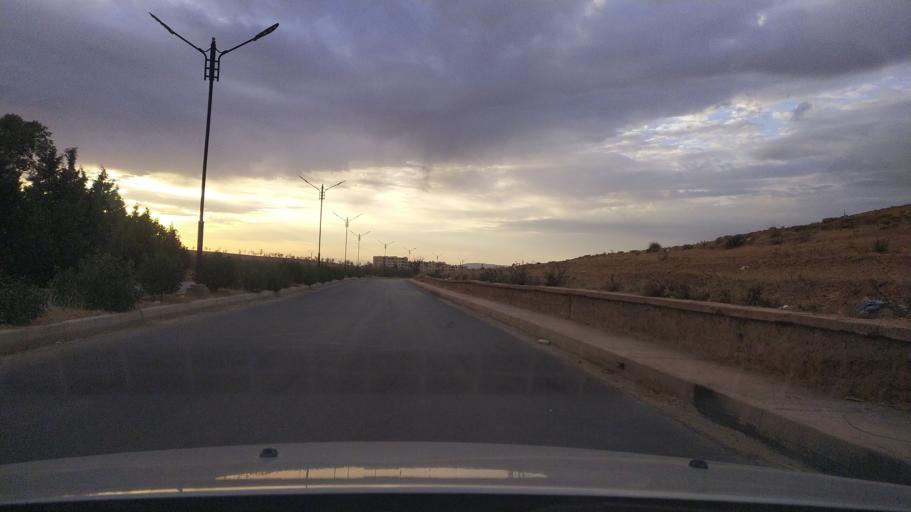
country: DZ
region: Tiaret
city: Frenda
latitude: 35.0515
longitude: 1.0696
